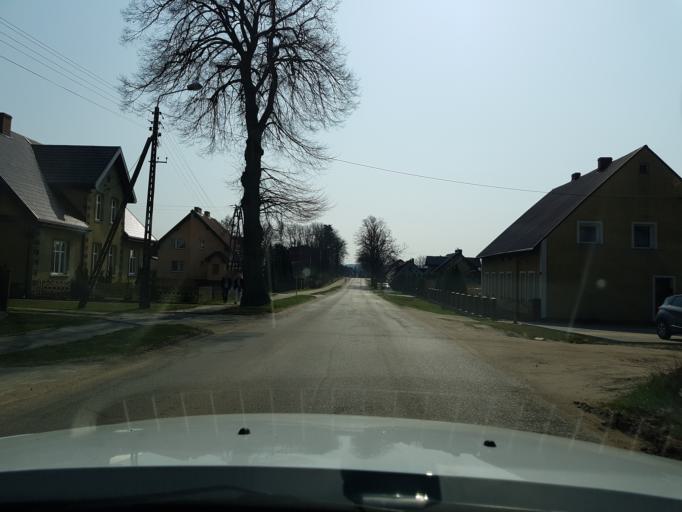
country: PL
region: West Pomeranian Voivodeship
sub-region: Powiat koszalinski
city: Sianow
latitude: 54.2348
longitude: 16.2988
